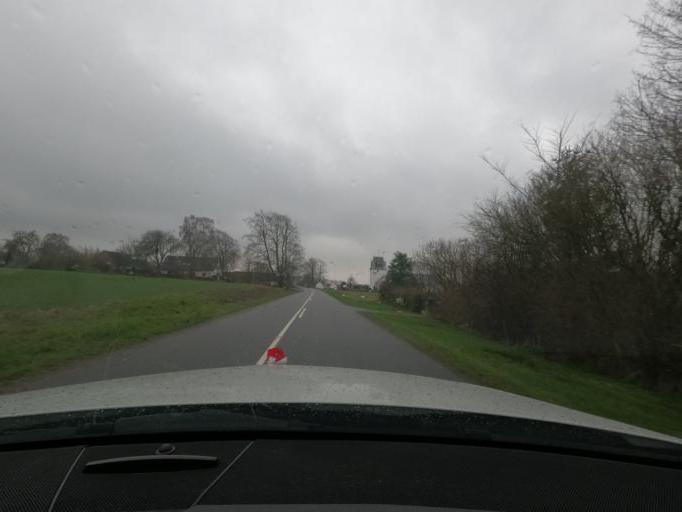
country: DK
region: South Denmark
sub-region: Haderslev Kommune
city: Starup
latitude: 55.2114
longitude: 9.6364
